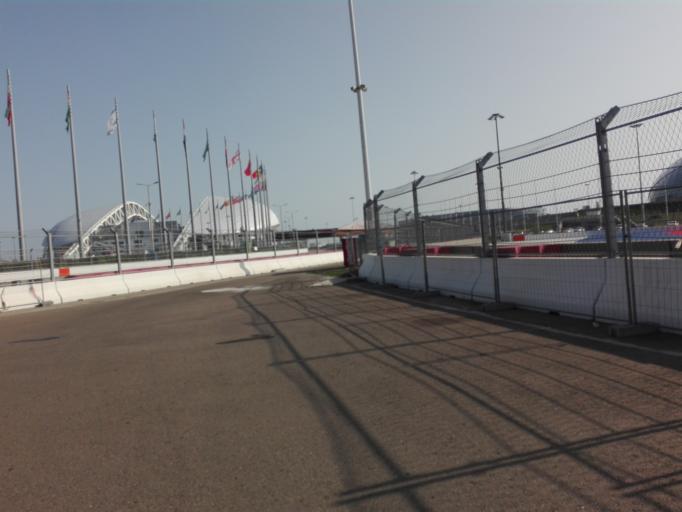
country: RU
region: Krasnodarskiy
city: Adler
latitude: 43.4072
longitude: 39.9520
